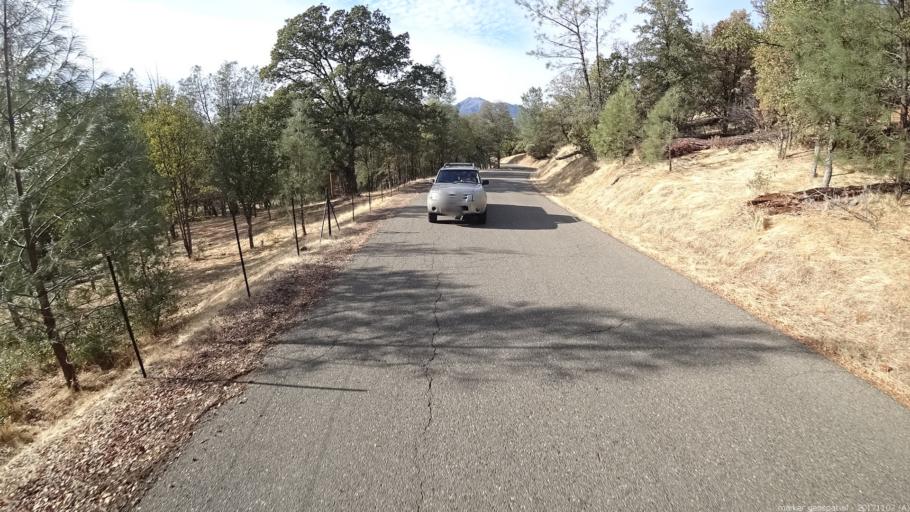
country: US
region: California
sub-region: Shasta County
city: Shasta
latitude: 40.5172
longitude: -122.5208
